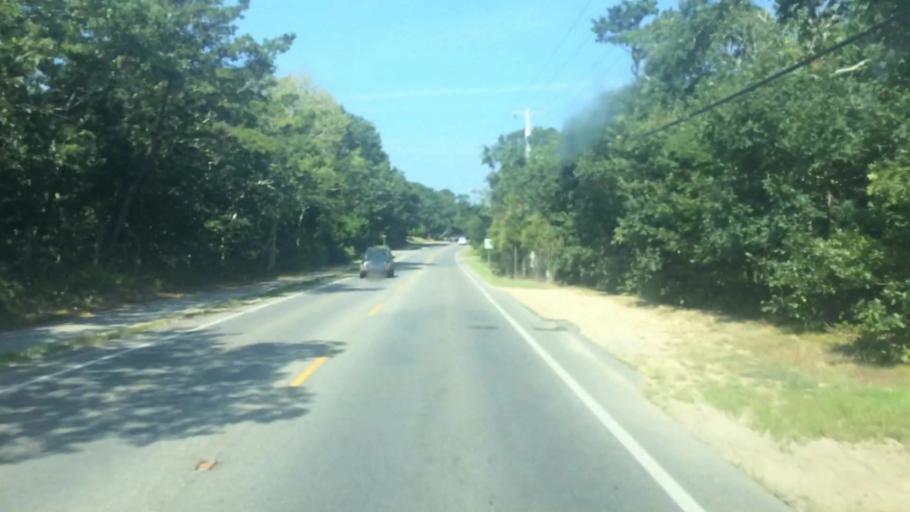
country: US
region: Massachusetts
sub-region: Dukes County
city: Oak Bluffs
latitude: 41.4092
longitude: -70.5696
